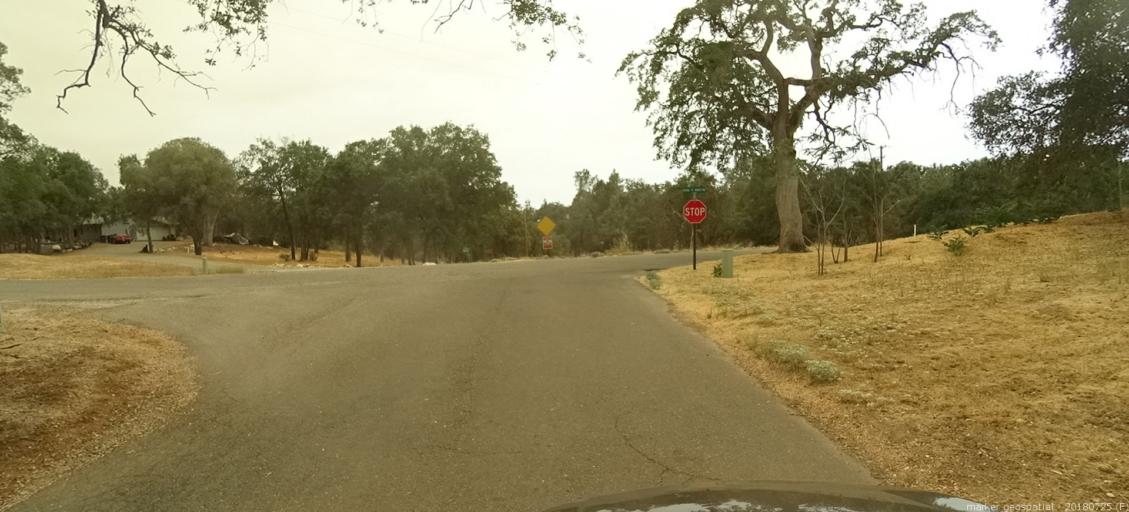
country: US
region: California
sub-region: Madera County
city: Coarsegold
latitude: 37.1923
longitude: -119.6733
